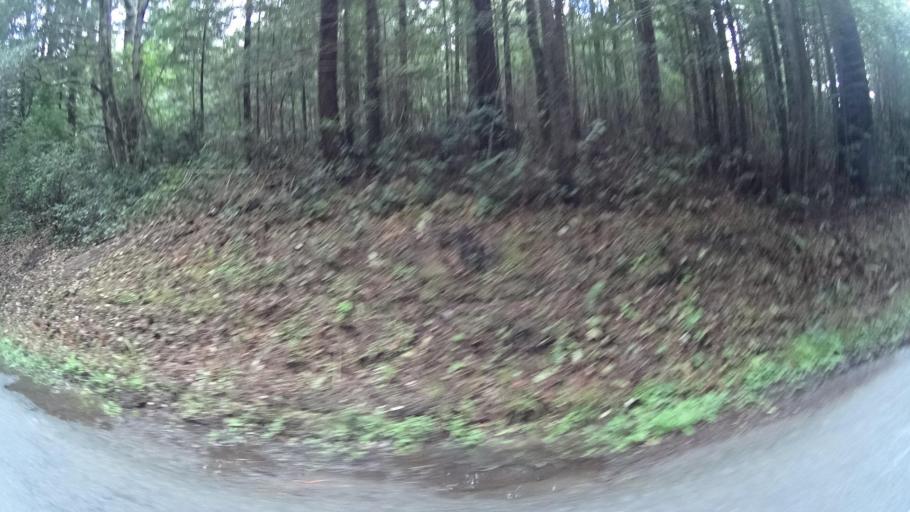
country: US
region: California
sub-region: Humboldt County
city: Blue Lake
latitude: 40.8196
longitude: -123.9976
